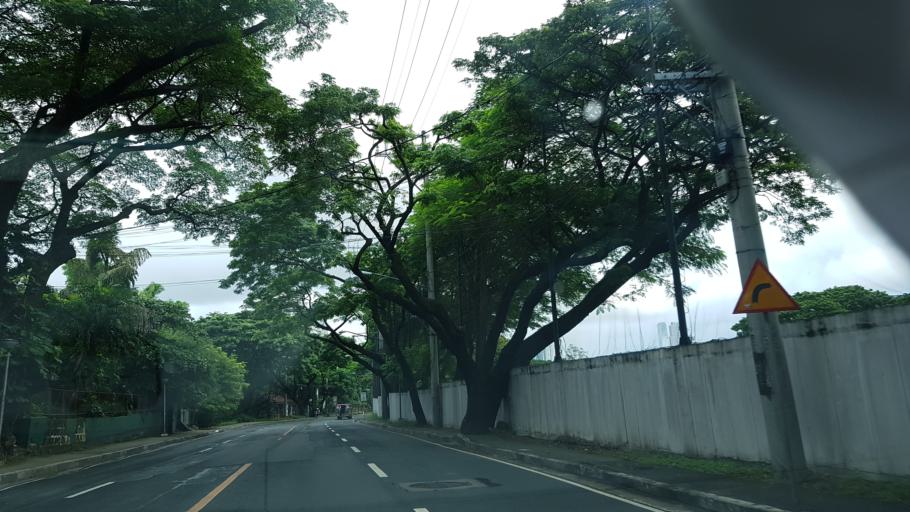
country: PH
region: Metro Manila
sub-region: Makati City
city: Makati City
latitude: 14.5451
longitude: 121.0433
